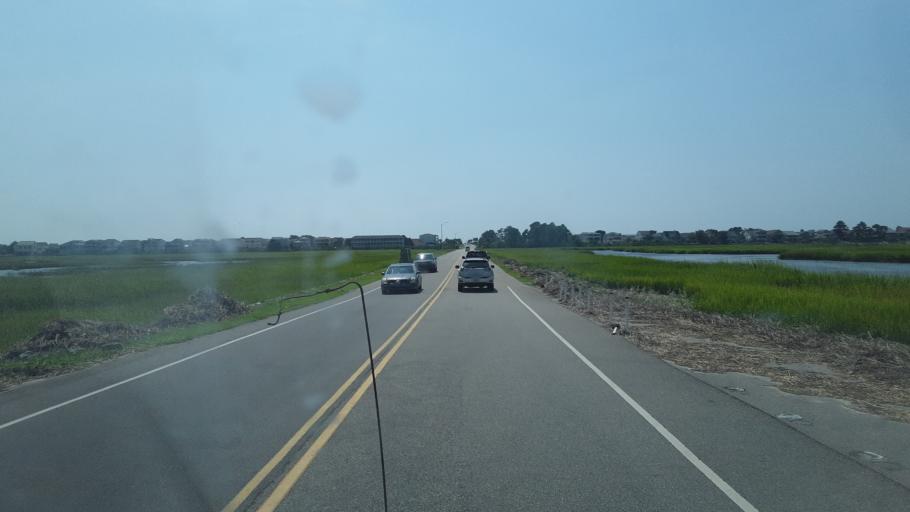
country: US
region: North Carolina
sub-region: Brunswick County
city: Sunset Beach
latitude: 33.8770
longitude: -78.5097
